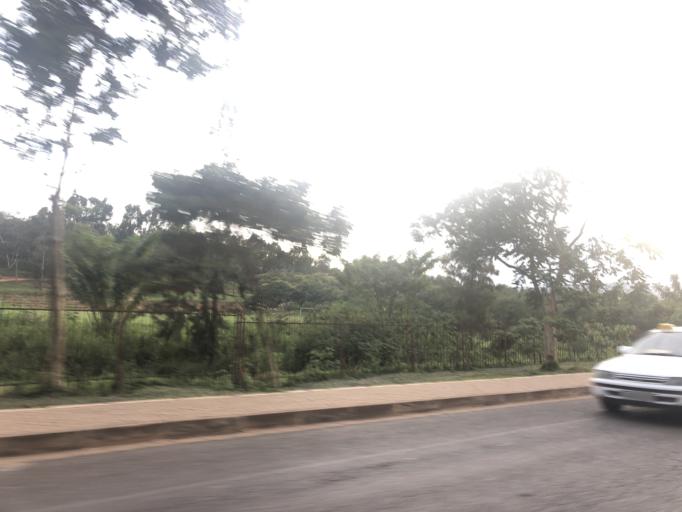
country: RW
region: Kigali
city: Kigali
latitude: -1.9295
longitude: 30.0800
